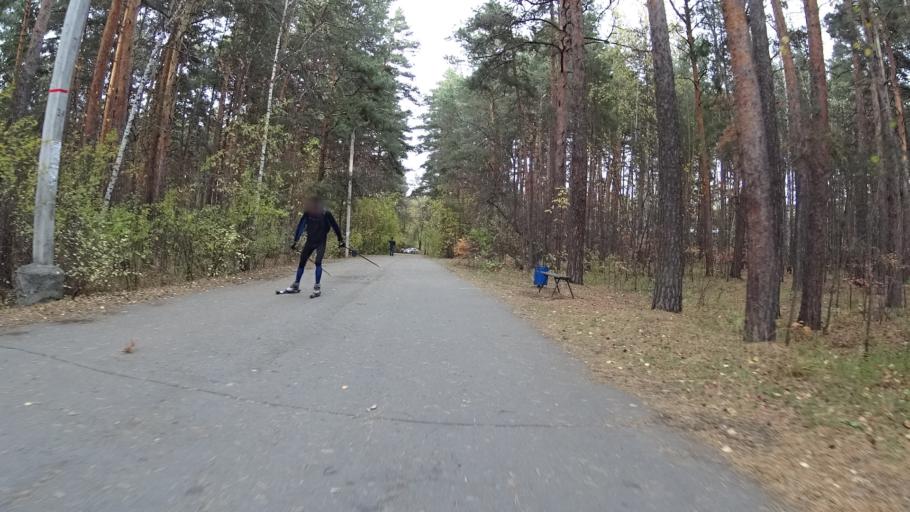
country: RU
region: Chelyabinsk
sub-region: Gorod Chelyabinsk
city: Chelyabinsk
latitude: 55.1541
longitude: 61.3595
